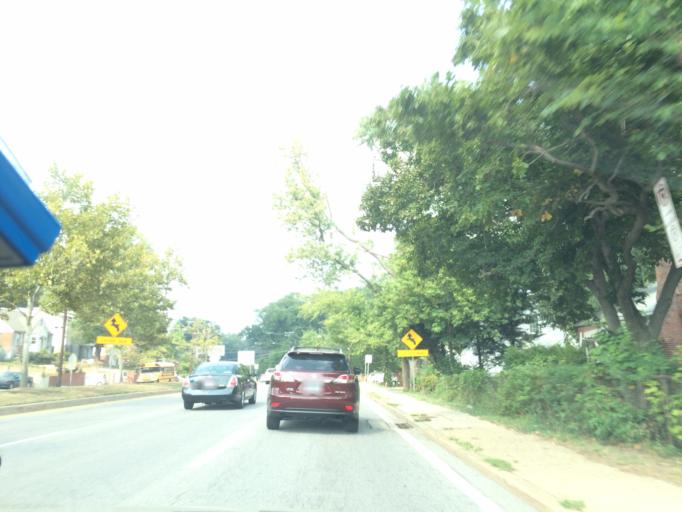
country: US
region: Maryland
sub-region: Montgomery County
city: Four Corners
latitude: 39.0222
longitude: -77.0116
